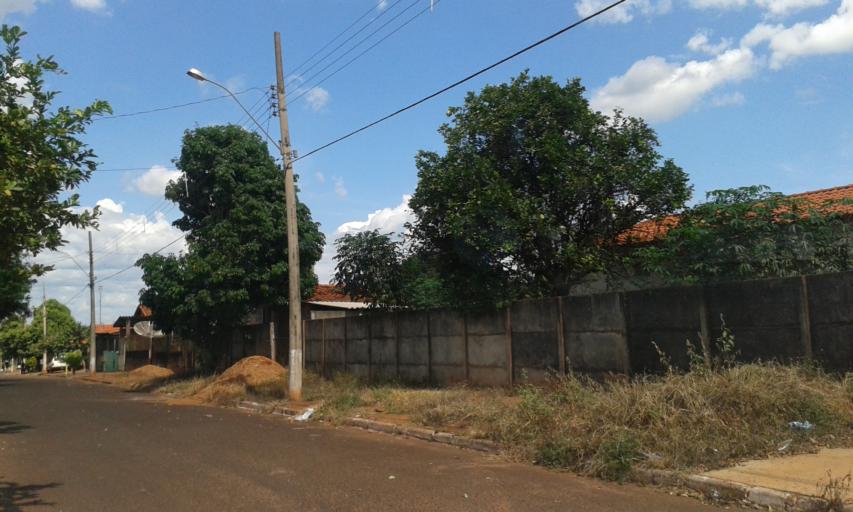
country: BR
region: Minas Gerais
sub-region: Santa Vitoria
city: Santa Vitoria
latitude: -18.8436
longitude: -50.1171
